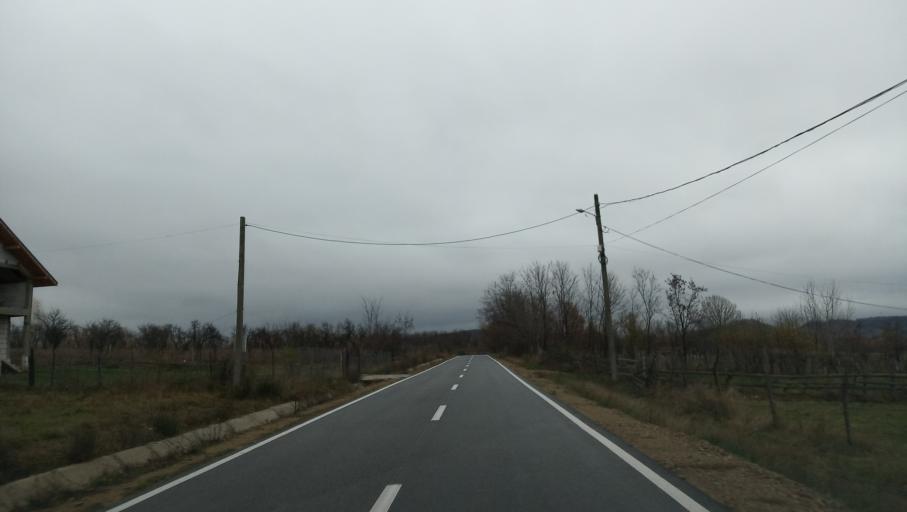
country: RO
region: Gorj
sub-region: Novaci
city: Pociovalistea
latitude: 45.1630
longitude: 23.6156
